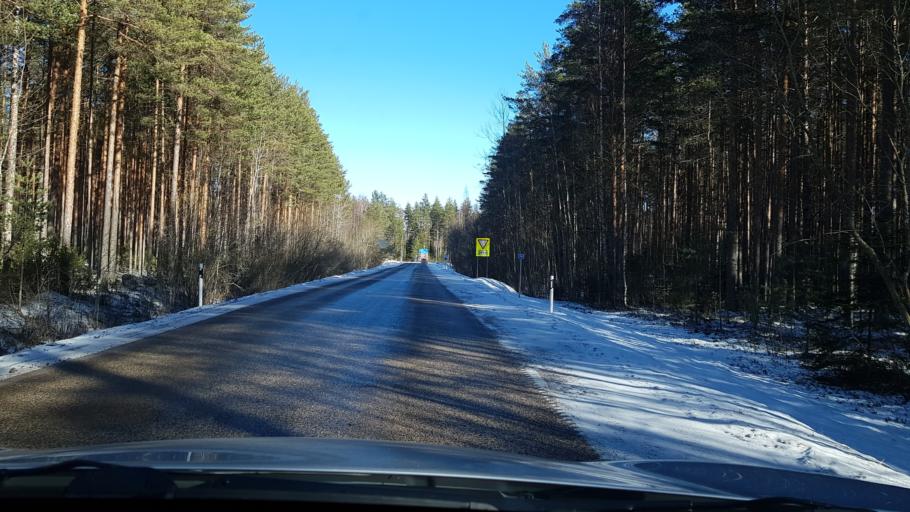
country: EE
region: Polvamaa
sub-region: Raepina vald
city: Rapina
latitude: 57.9760
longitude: 27.5695
